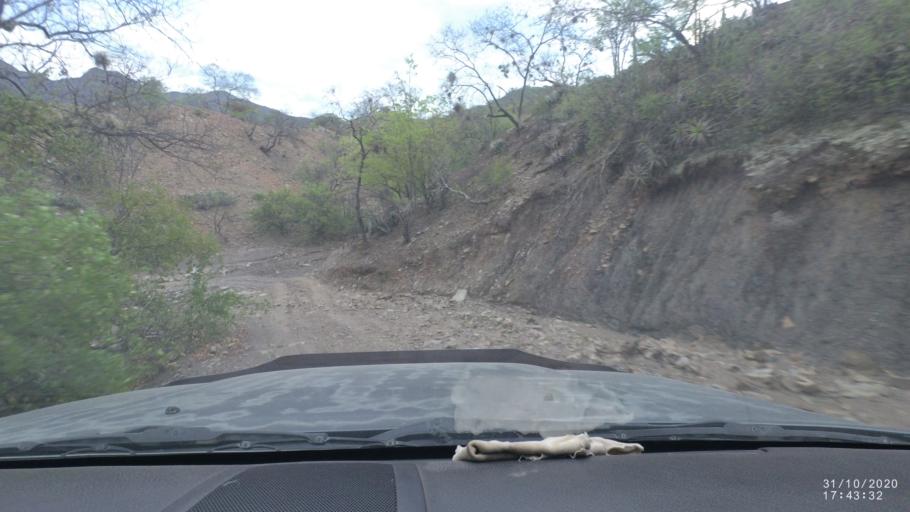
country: BO
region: Chuquisaca
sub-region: Provincia Zudanez
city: Mojocoya
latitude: -18.6093
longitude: -64.5479
